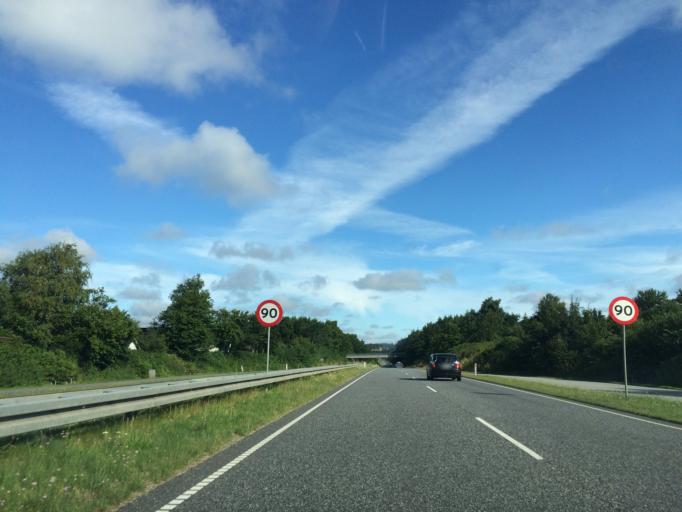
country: DK
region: Central Jutland
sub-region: Viborg Kommune
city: Viborg
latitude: 56.3959
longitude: 9.4411
